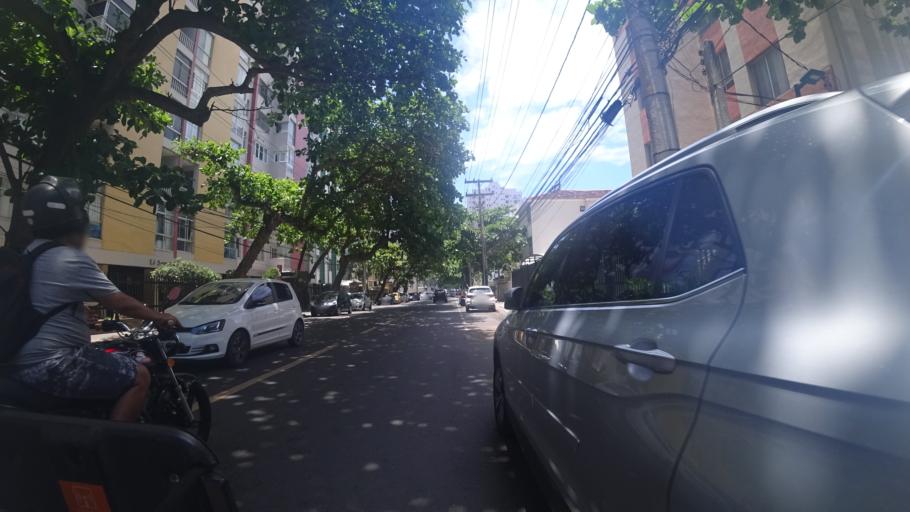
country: BR
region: Bahia
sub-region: Salvador
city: Salvador
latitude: -13.0081
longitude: -38.4655
